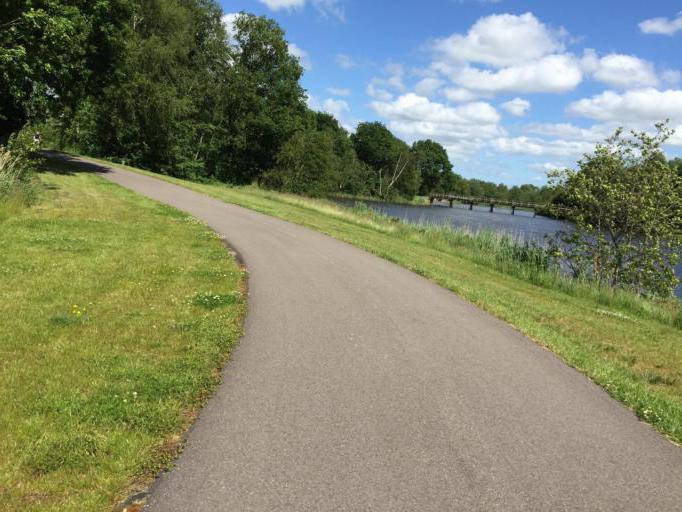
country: NL
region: Friesland
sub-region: Gemeente Leeuwarden
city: Camminghaburen
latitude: 53.2127
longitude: 5.8703
